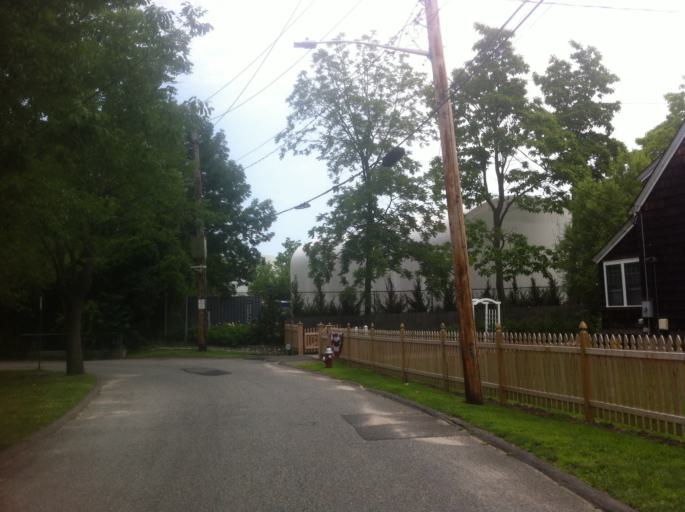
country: US
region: New York
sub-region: Nassau County
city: Oyster Bay
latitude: 40.8735
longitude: -73.5284
